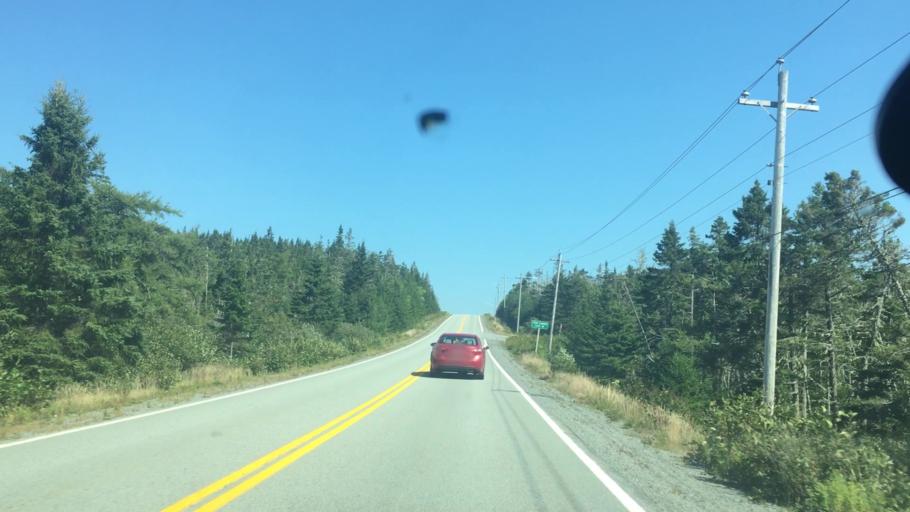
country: CA
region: Nova Scotia
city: Antigonish
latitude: 44.9367
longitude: -62.2701
